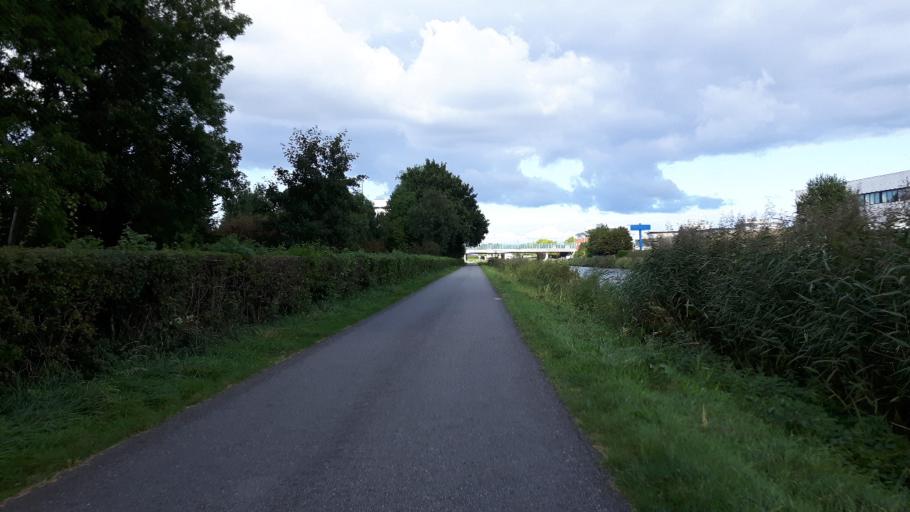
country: NL
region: Utrecht
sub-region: Gemeente Vianen
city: Vianen
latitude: 51.9786
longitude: 5.0887
